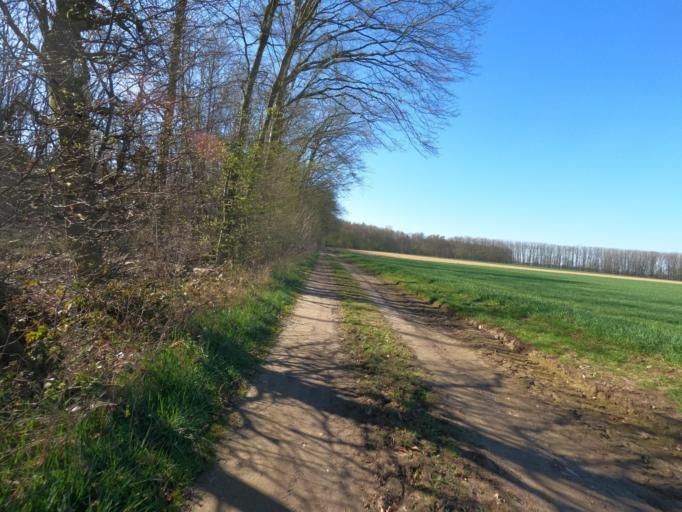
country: DE
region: North Rhine-Westphalia
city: Geilenkirchen
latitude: 51.0054
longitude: 6.1479
